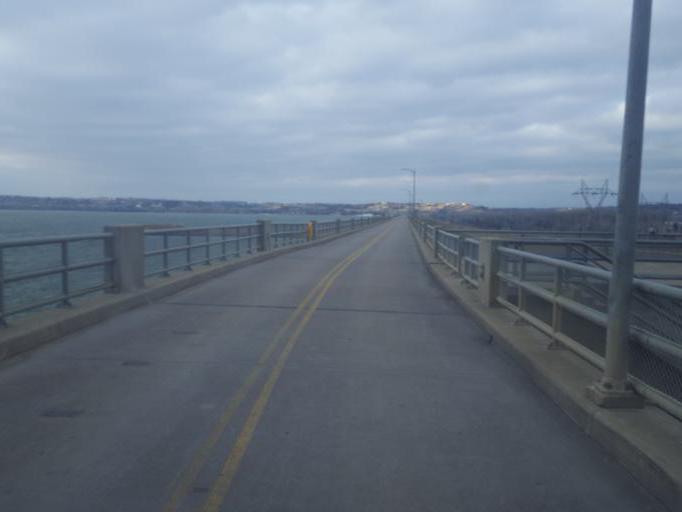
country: US
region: South Dakota
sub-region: Yankton County
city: Yankton
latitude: 42.8496
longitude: -97.4821
